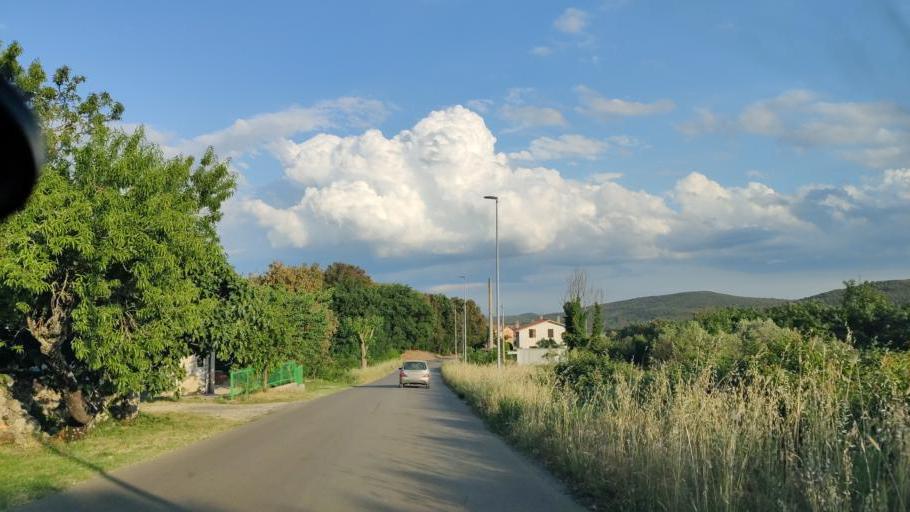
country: IT
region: Umbria
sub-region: Provincia di Terni
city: Lugnano in Teverina
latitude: 42.5977
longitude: 12.3664
